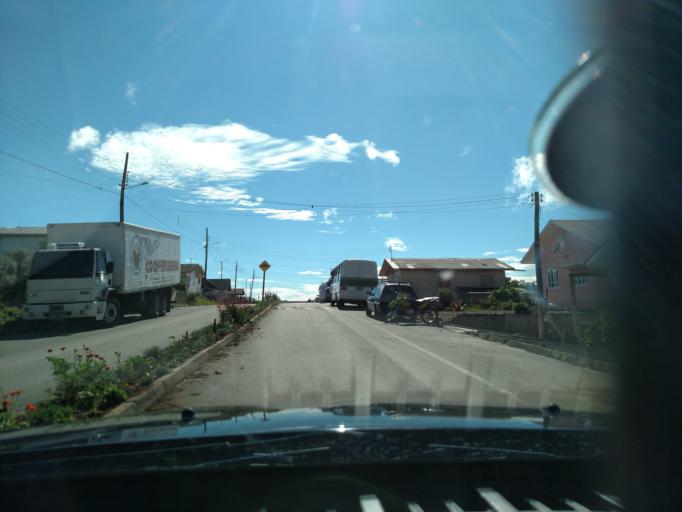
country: BR
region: Santa Catarina
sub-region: Sao Joaquim
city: Sao Joaquim
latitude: -28.2900
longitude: -49.9226
